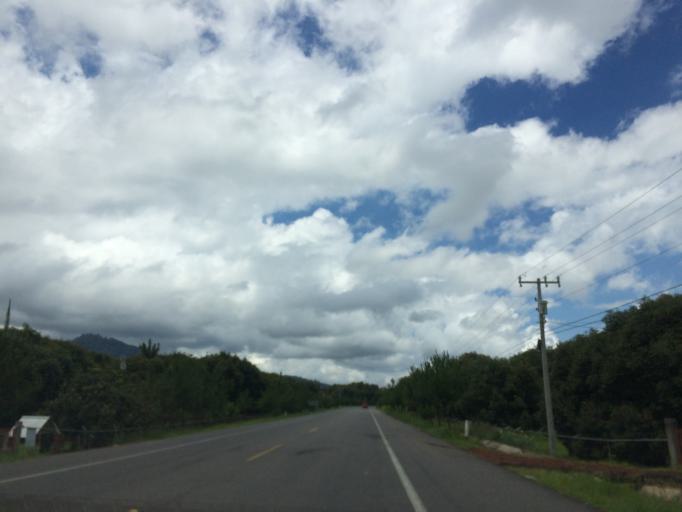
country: MX
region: Michoacan
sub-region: Uruapan
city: Santa Ana Zirosto
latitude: 19.5437
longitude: -102.3225
